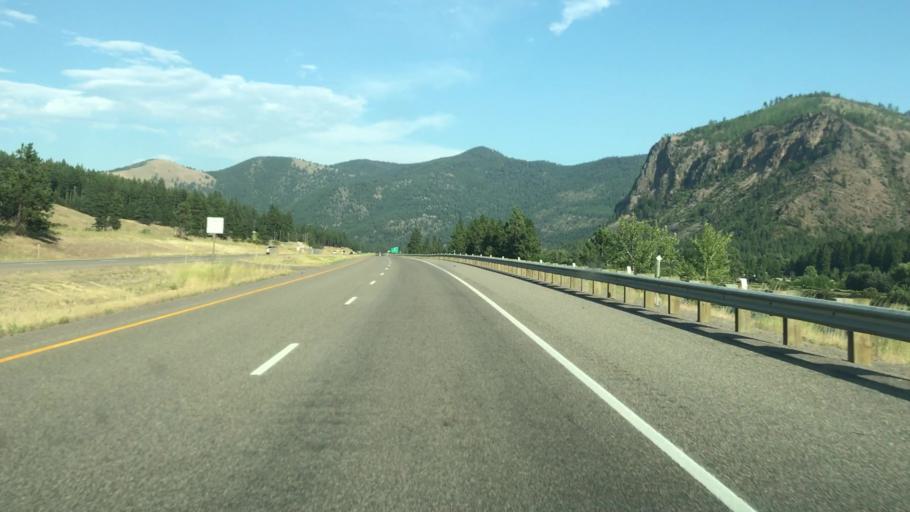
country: US
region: Montana
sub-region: Missoula County
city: Frenchtown
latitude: 46.9965
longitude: -114.4600
